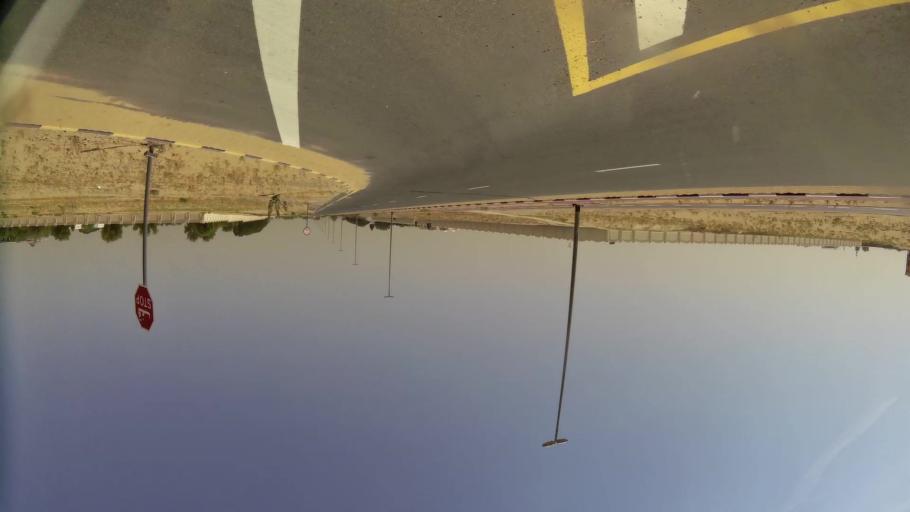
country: AE
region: Ajman
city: Ajman
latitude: 25.4025
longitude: 55.5381
